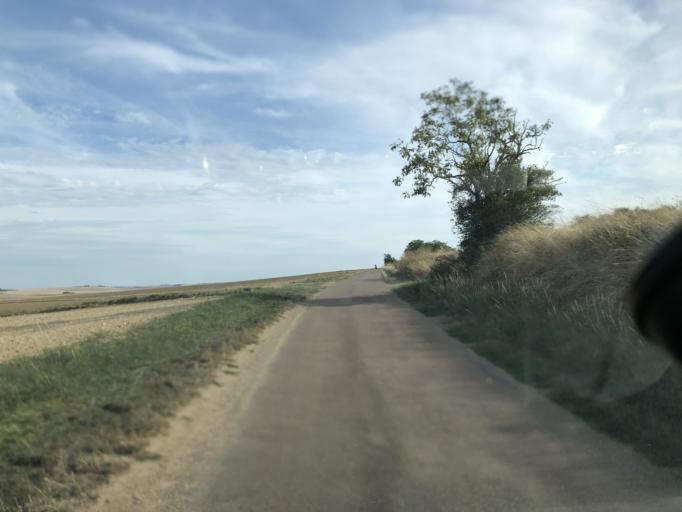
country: FR
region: Bourgogne
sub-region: Departement de l'Yonne
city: Joigny
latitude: 47.9372
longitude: 3.3873
